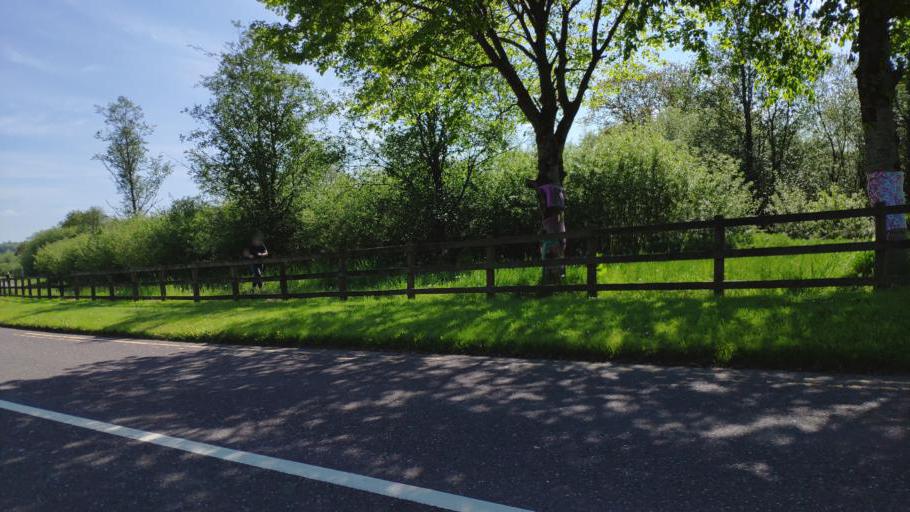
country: IE
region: Munster
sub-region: County Cork
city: Blarney
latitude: 51.9286
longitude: -8.5569
